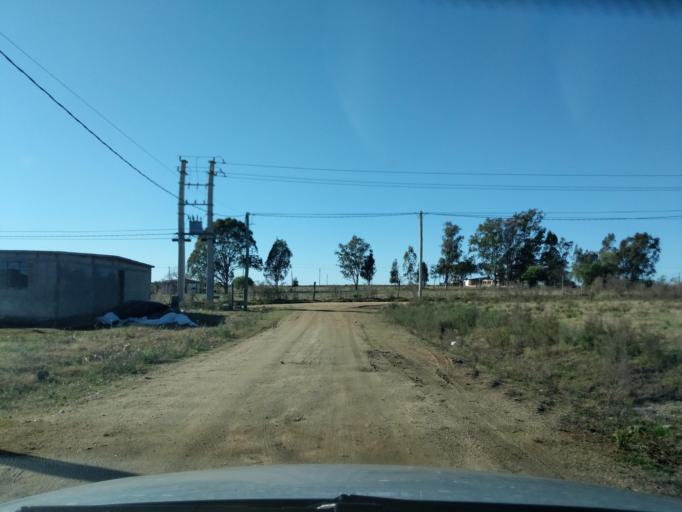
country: UY
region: Florida
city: Florida
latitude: -34.0823
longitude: -56.2389
